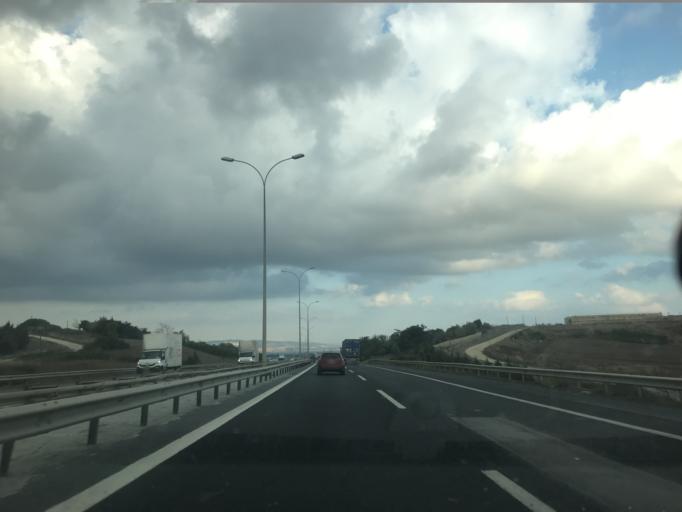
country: TR
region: Istanbul
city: Bueyuekcekmece
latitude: 41.0975
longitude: 28.6190
